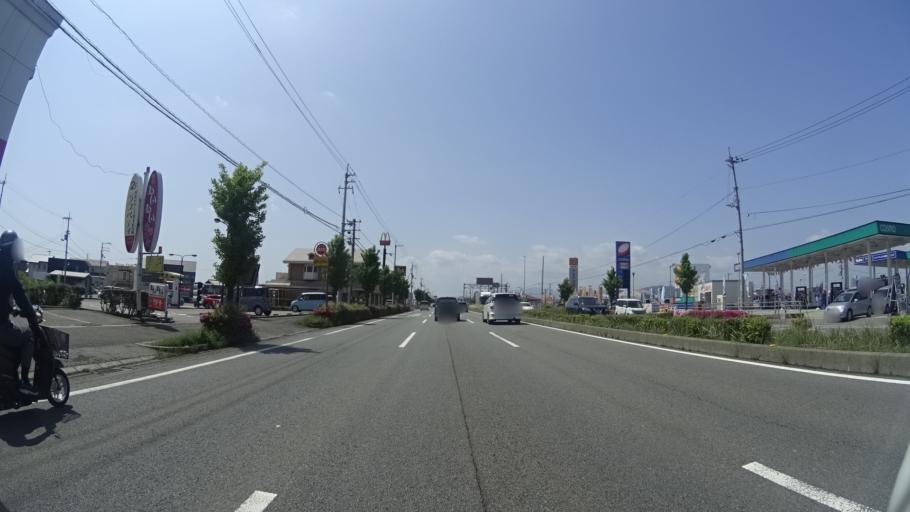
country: JP
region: Tokushima
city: Tokushima-shi
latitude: 34.1114
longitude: 134.5772
